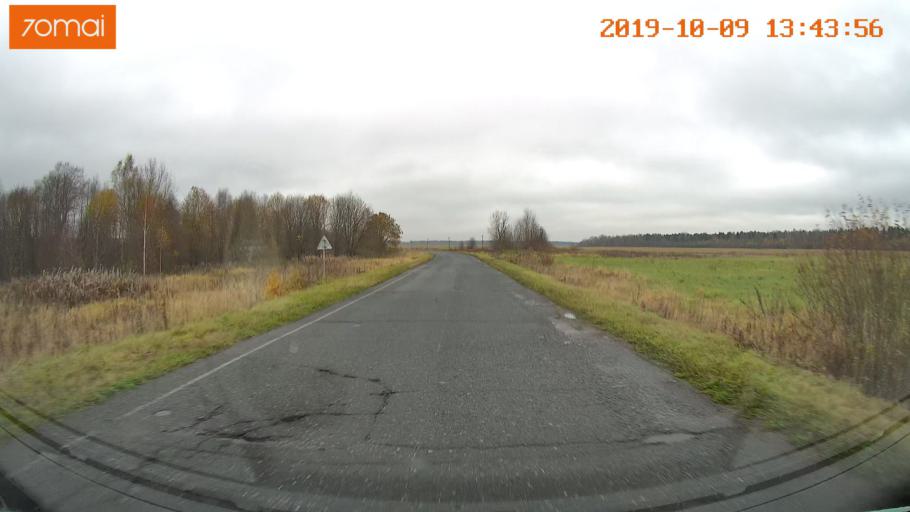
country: RU
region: Kostroma
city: Buy
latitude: 58.3617
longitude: 41.2054
